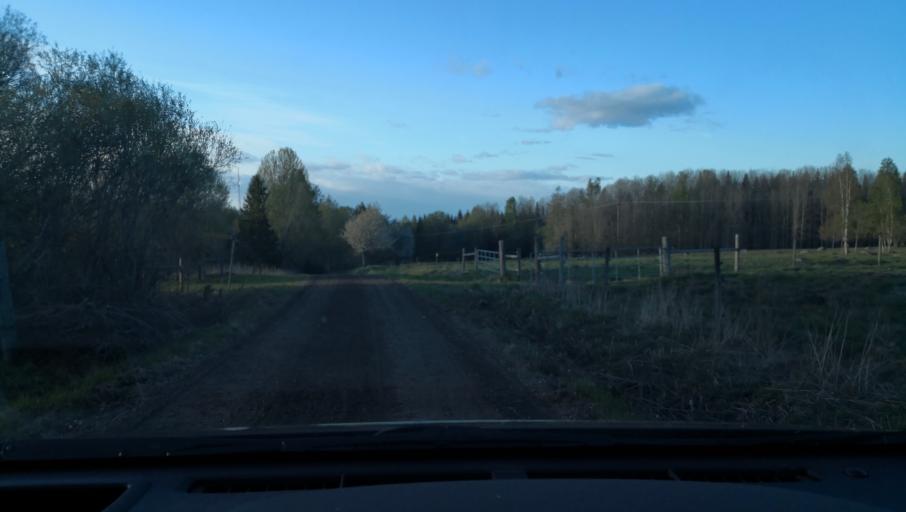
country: SE
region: OErebro
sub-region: Askersunds Kommun
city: Asbro
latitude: 58.8710
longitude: 15.1436
